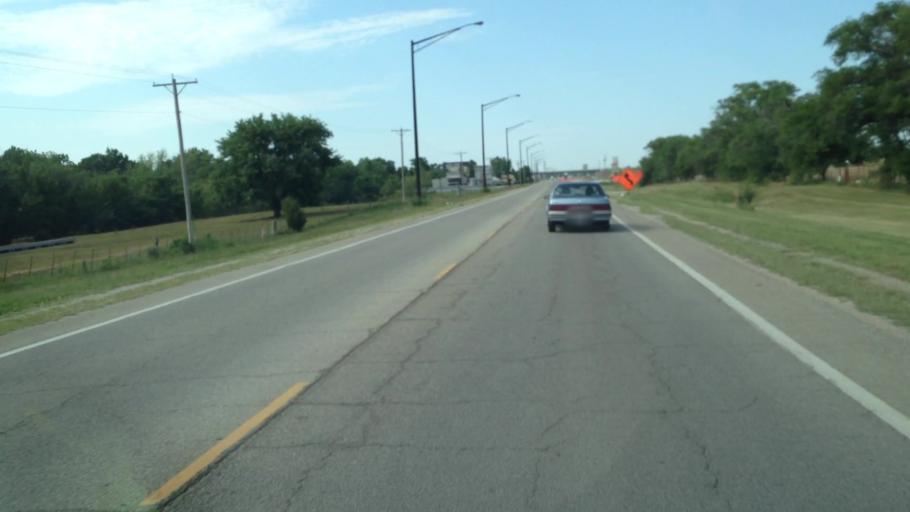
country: US
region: Kansas
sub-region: Labette County
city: Parsons
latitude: 37.3590
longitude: -95.2586
